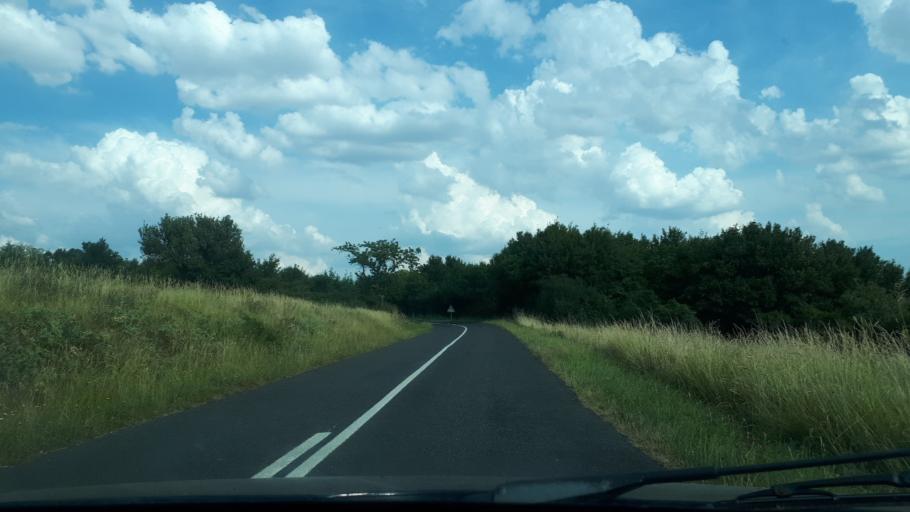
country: FR
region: Pays de la Loire
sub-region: Departement de la Sarthe
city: Besse-sur-Braye
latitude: 47.7779
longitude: 0.7886
